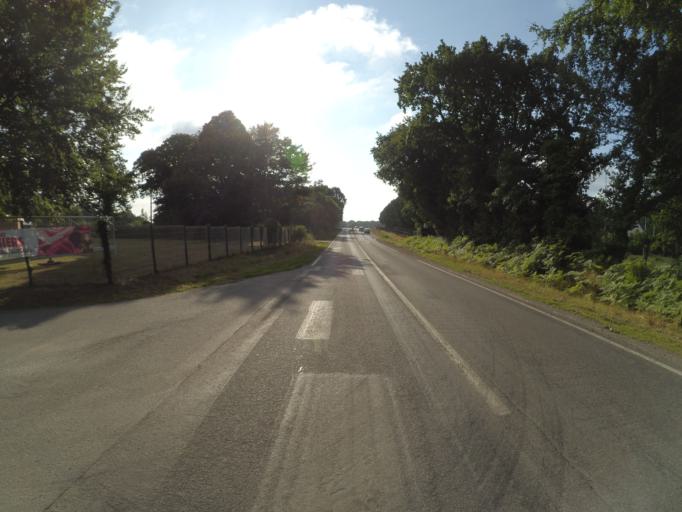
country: FR
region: Brittany
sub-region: Departement du Morbihan
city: Queven
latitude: 47.7801
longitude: -3.4386
